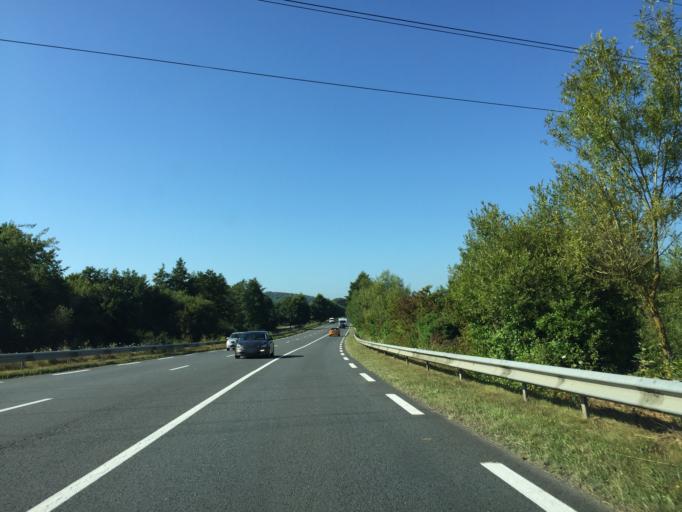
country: FR
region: Lower Normandy
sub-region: Departement du Calvados
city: Lisieux
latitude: 49.2192
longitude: 0.2226
